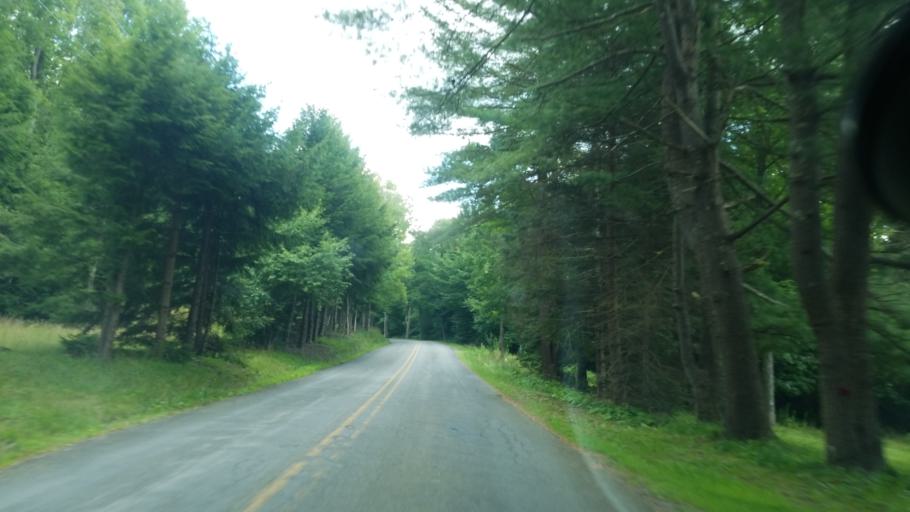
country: US
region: Pennsylvania
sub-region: Jefferson County
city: Brookville
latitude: 41.2309
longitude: -79.0621
